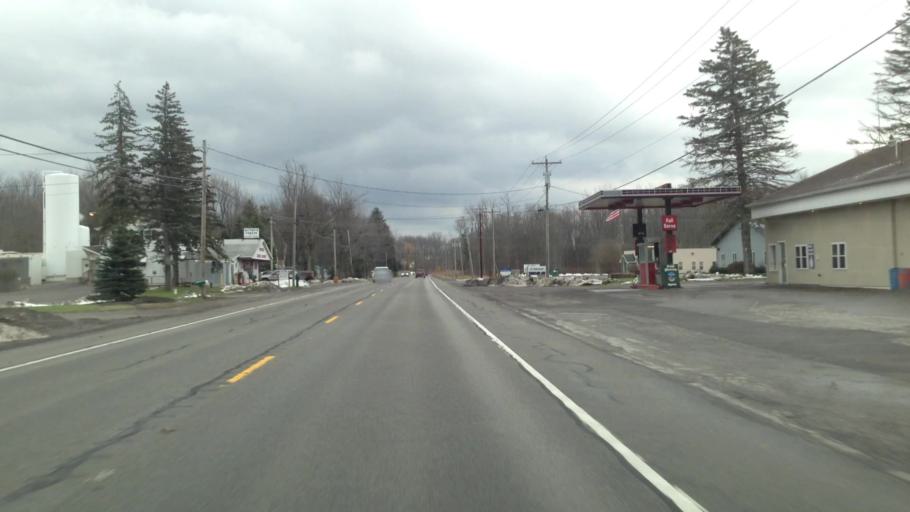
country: US
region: New York
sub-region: Erie County
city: Akron
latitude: 42.9944
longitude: -78.4244
